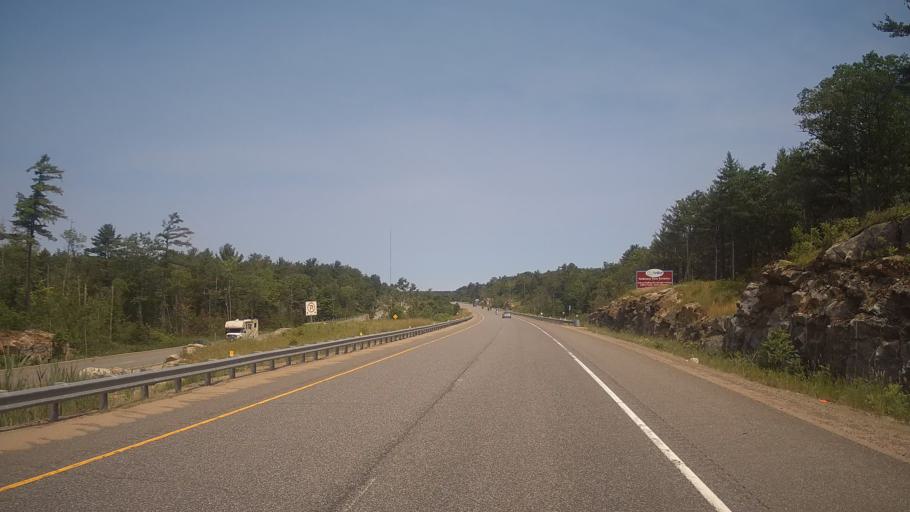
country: CA
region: Ontario
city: Midland
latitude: 44.9342
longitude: -79.7746
